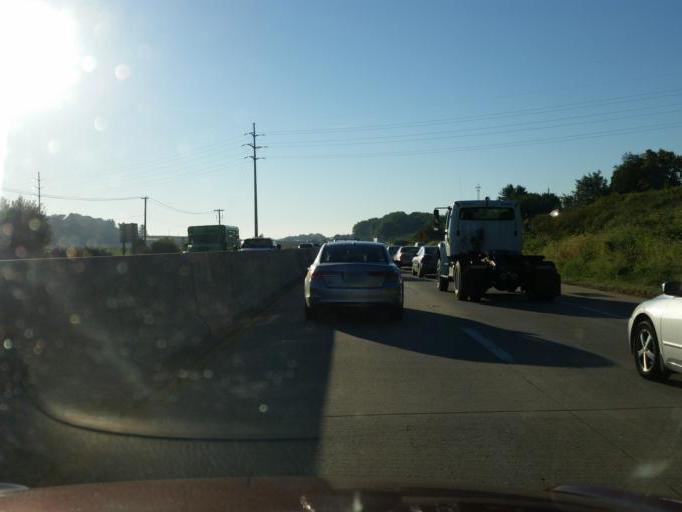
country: US
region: Pennsylvania
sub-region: Lancaster County
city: East Petersburg
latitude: 40.0885
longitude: -76.3798
